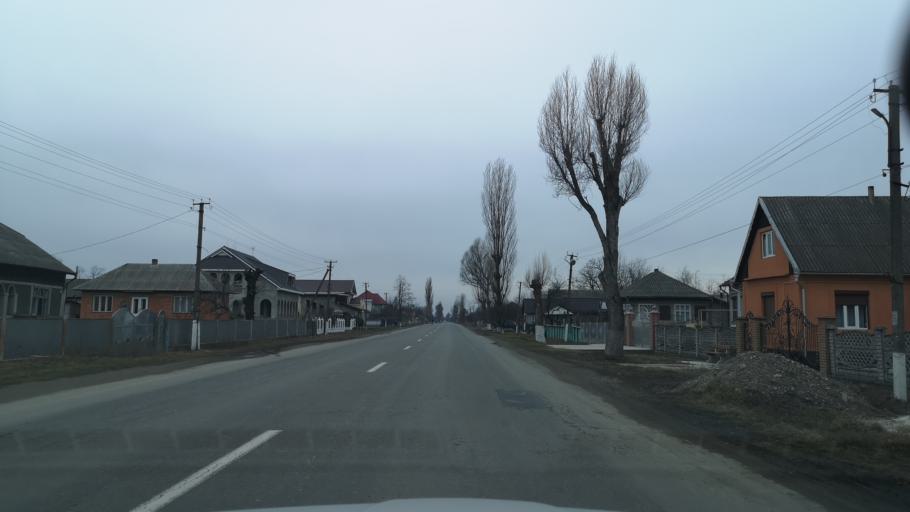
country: RO
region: Botosani
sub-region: Comuna Darabani
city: Bajura
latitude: 48.2317
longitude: 26.5386
